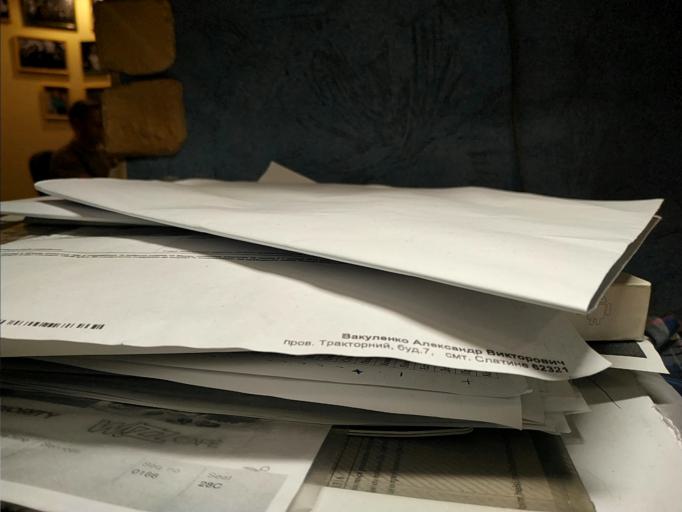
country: RU
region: Tverskaya
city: Zubtsov
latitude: 56.1193
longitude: 34.5785
